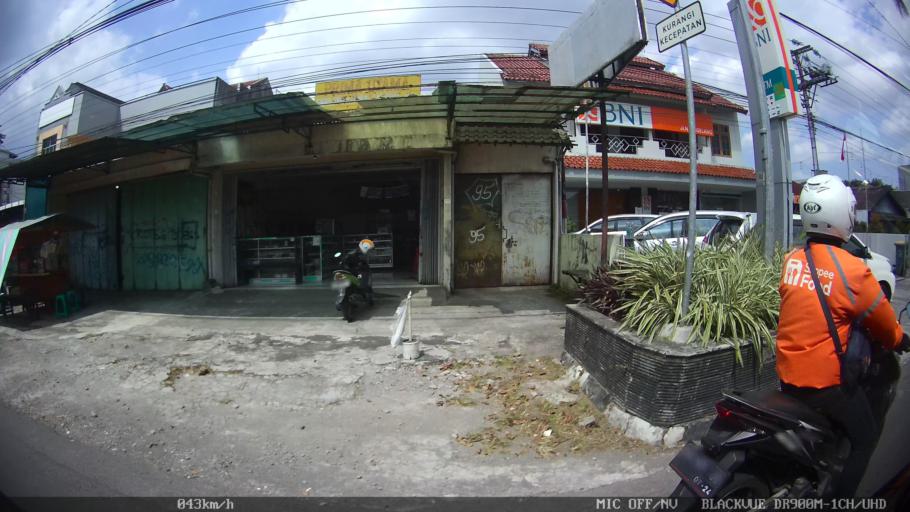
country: ID
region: Daerah Istimewa Yogyakarta
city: Yogyakarta
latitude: -7.7602
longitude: 110.3621
